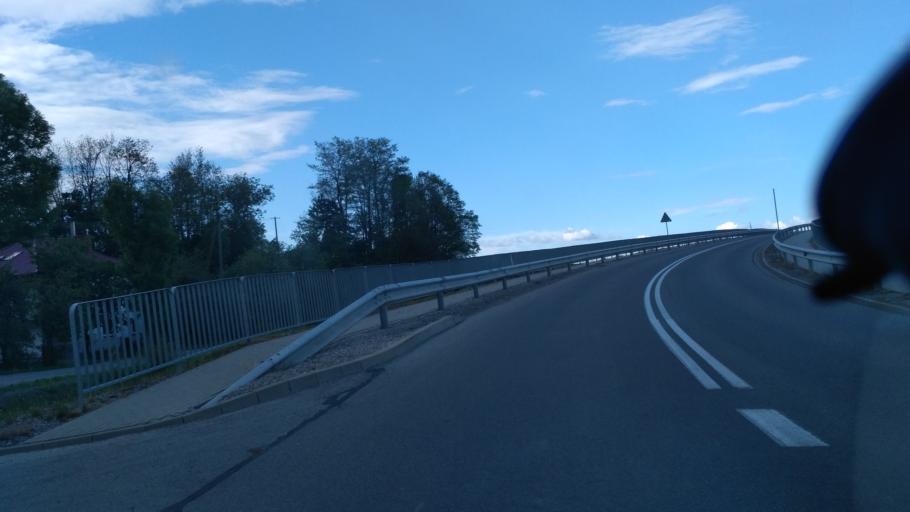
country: PL
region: Subcarpathian Voivodeship
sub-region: Powiat jaroslawski
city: Rokietnica
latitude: 49.9432
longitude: 22.6663
